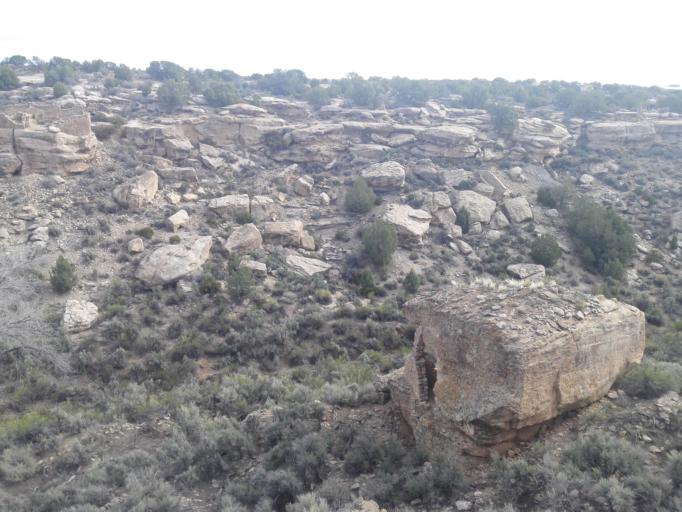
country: US
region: Colorado
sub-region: Montezuma County
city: Towaoc
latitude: 37.3833
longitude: -109.0774
